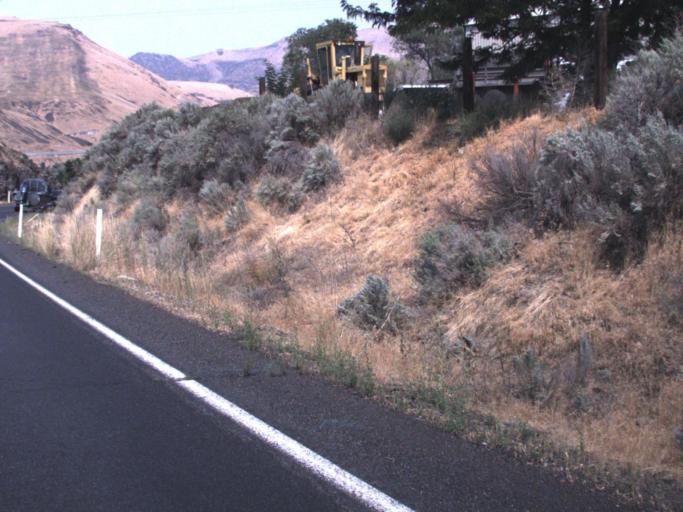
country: US
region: Washington
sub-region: Yakima County
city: Selah
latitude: 46.7035
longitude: -120.4735
